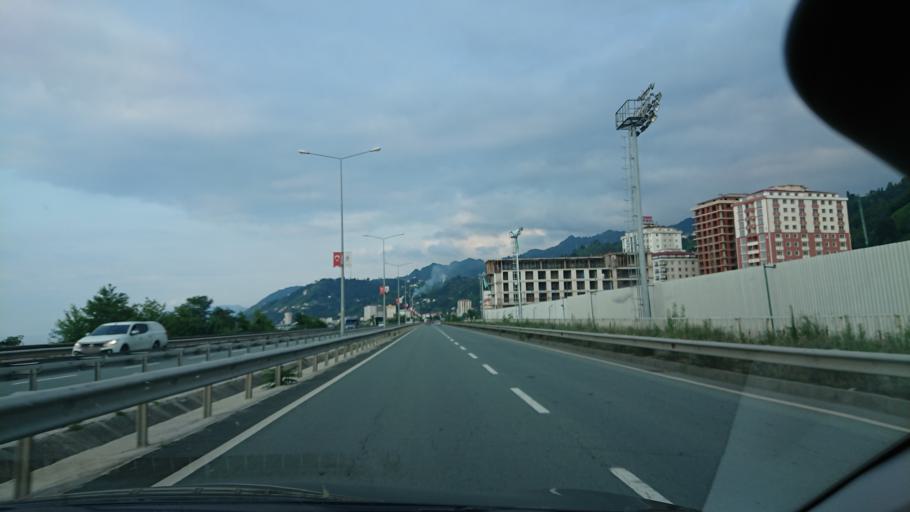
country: TR
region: Rize
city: Gundogdu
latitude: 41.0472
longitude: 40.5878
